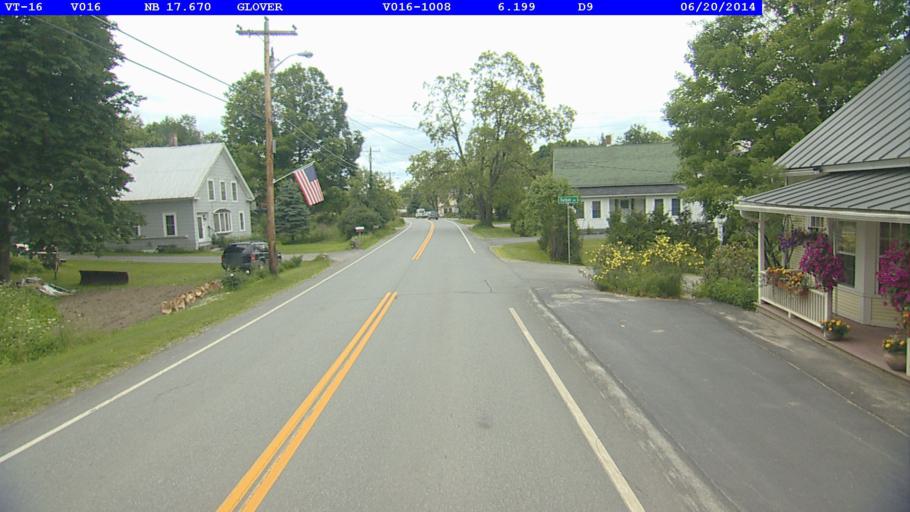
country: US
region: Vermont
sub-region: Orleans County
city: Newport
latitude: 44.7102
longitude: -72.1855
